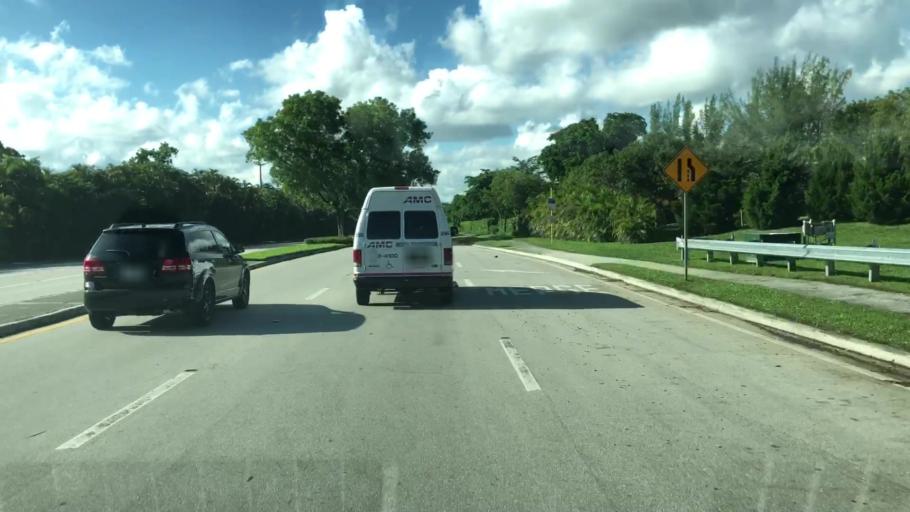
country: US
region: Florida
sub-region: Broward County
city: Coral Springs
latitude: 26.2583
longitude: -80.2660
